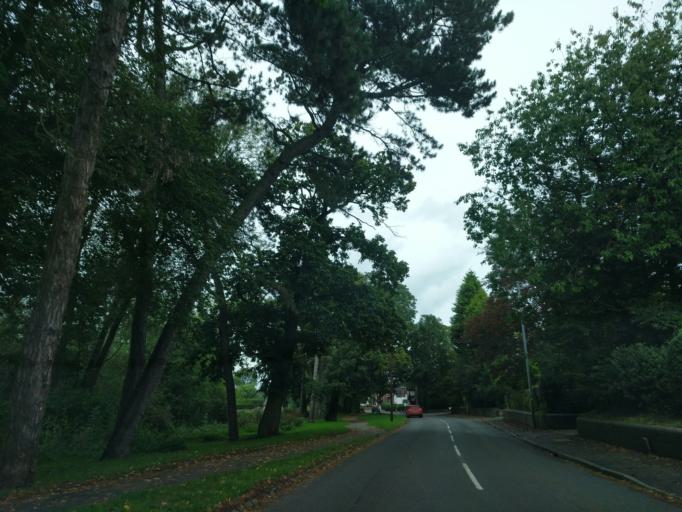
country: GB
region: England
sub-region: Staffordshire
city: Audley
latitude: 52.9990
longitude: -2.3399
